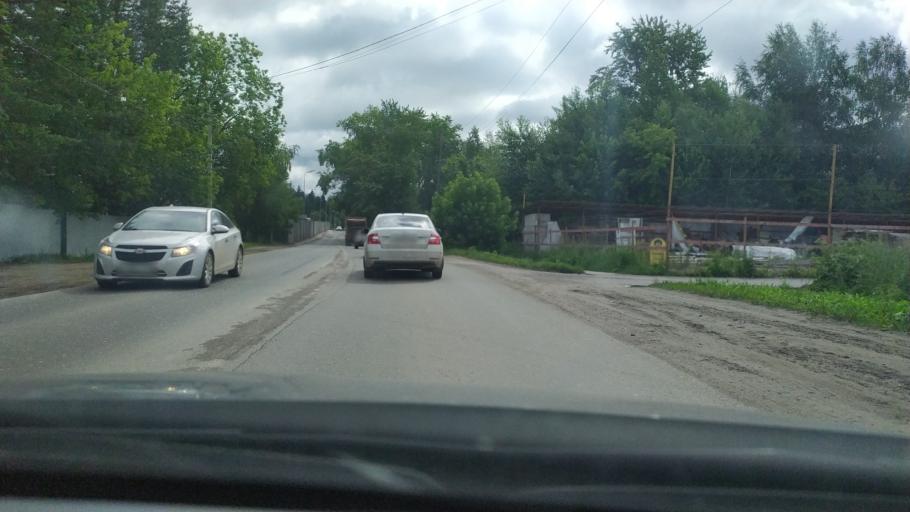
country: RU
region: Perm
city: Froly
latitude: 57.9762
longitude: 56.3165
